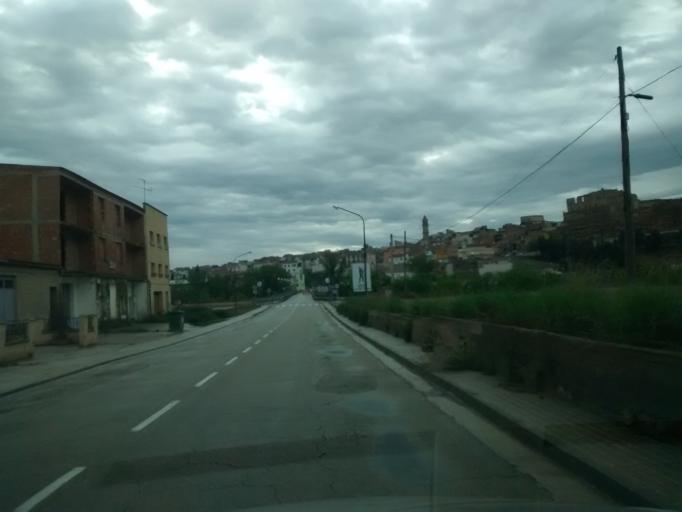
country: ES
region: Aragon
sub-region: Provincia de Zaragoza
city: Maella
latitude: 41.1186
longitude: 0.1438
